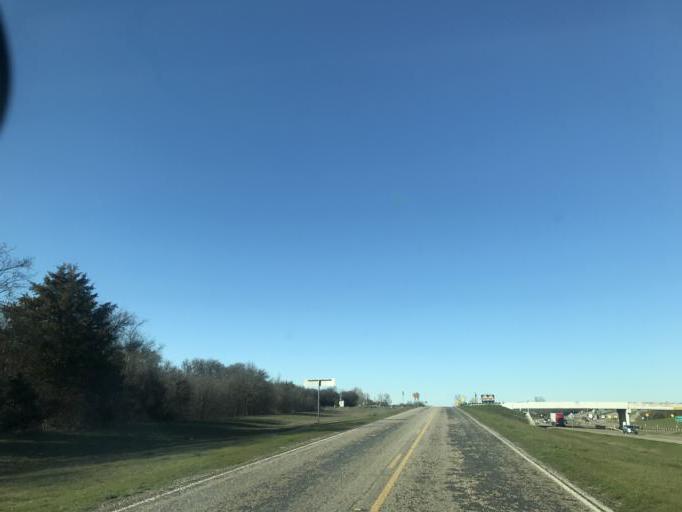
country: US
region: Texas
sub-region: Ellis County
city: Ferris
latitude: 32.5123
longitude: -96.6638
